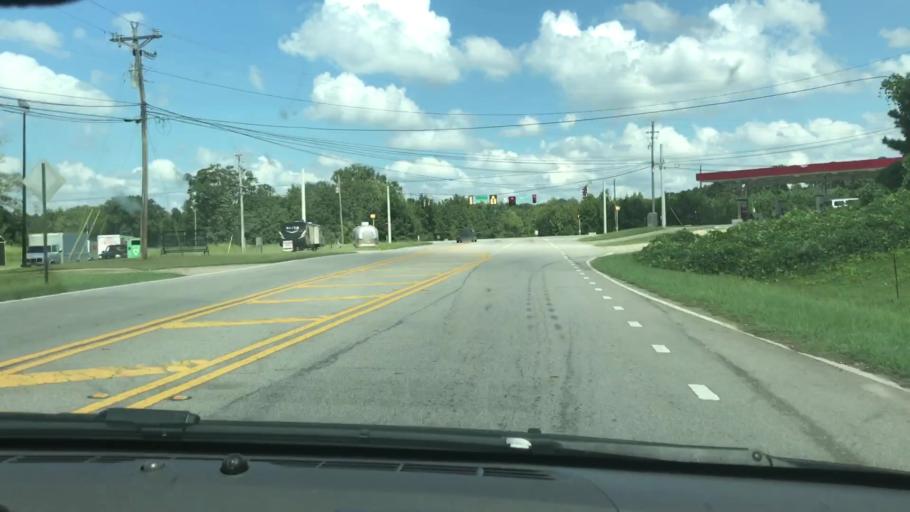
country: US
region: Georgia
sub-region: Troup County
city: La Grange
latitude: 33.0207
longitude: -85.0809
